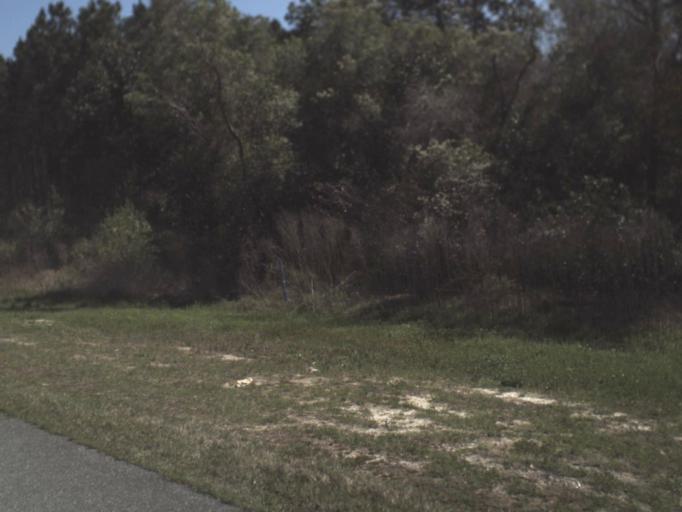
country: US
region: Florida
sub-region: Gulf County
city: Port Saint Joe
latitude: 29.8877
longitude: -85.3478
